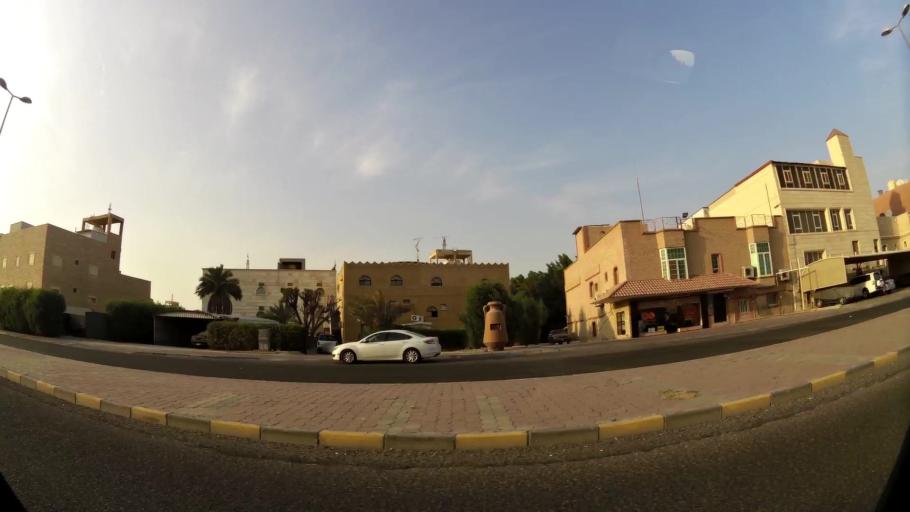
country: KW
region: Mubarak al Kabir
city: Sabah as Salim
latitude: 29.2498
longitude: 48.0698
